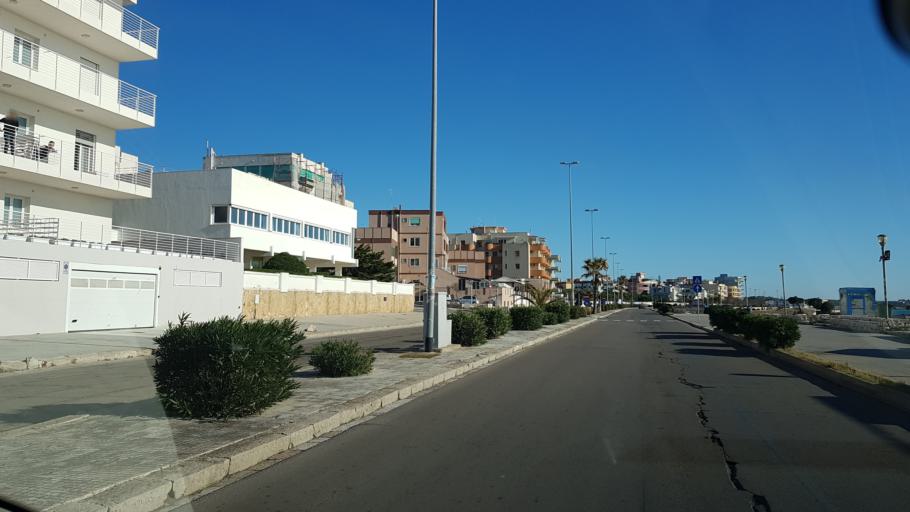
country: IT
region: Apulia
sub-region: Provincia di Lecce
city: Gallipoli
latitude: 40.0521
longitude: 17.9950
